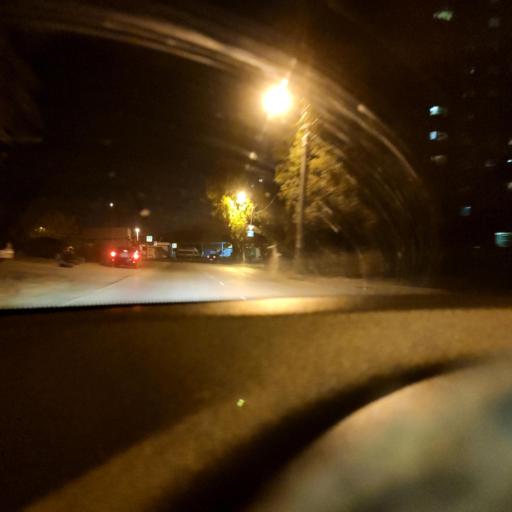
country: RU
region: Samara
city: Samara
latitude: 53.2449
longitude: 50.2545
